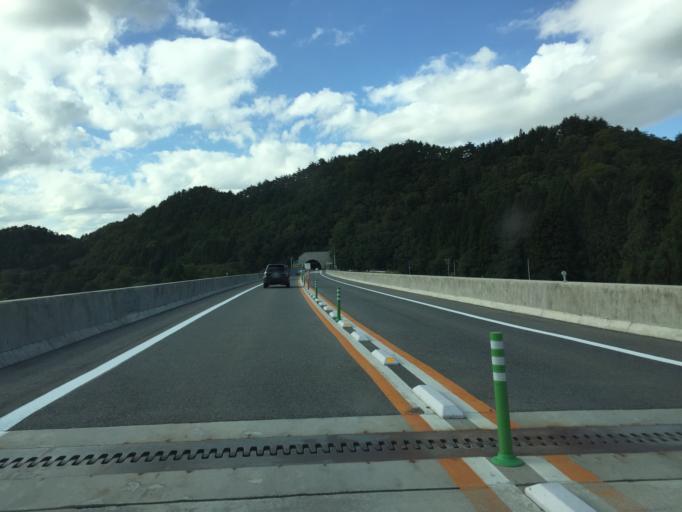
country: JP
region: Yamagata
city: Yonezawa
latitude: 37.8702
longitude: 140.2057
